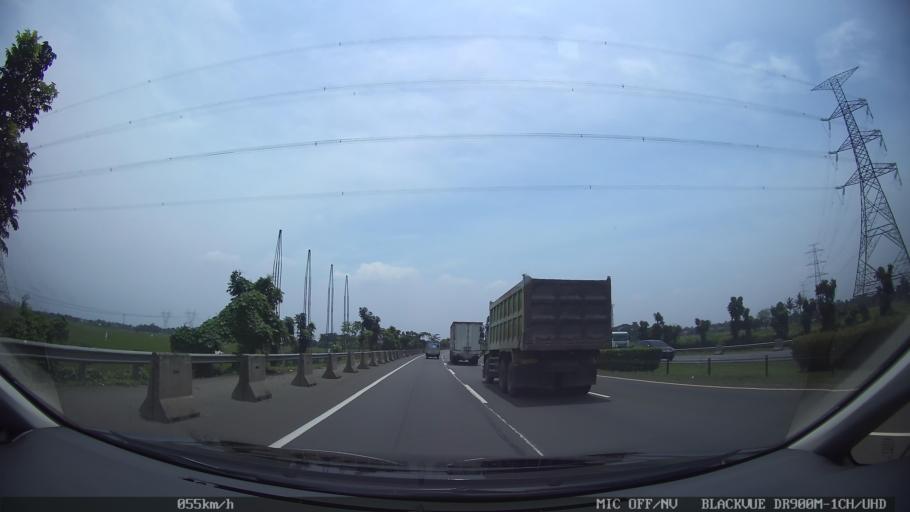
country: ID
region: West Java
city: Kresek
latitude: -6.1927
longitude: 106.4195
